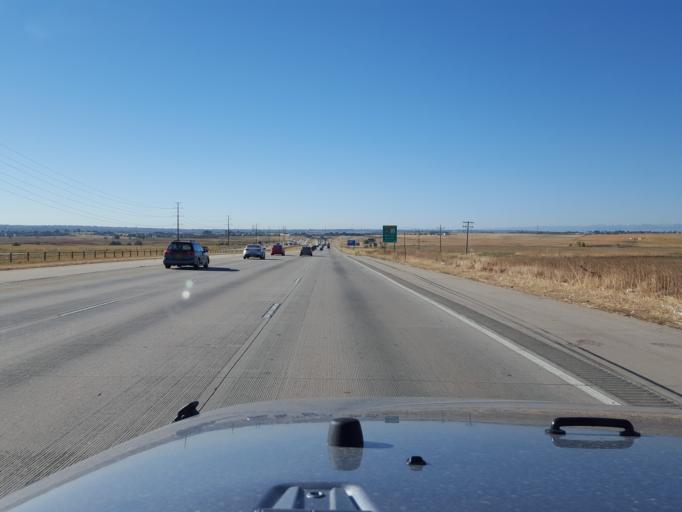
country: US
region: Colorado
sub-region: Boulder County
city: Erie
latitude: 40.0168
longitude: -104.9810
